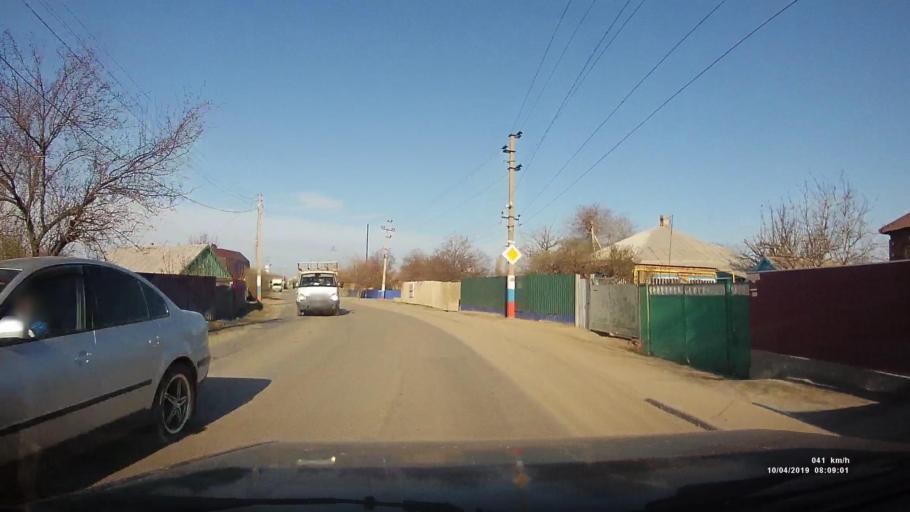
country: RU
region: Rostov
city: Staraya Stanitsa
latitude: 48.3495
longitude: 40.2810
